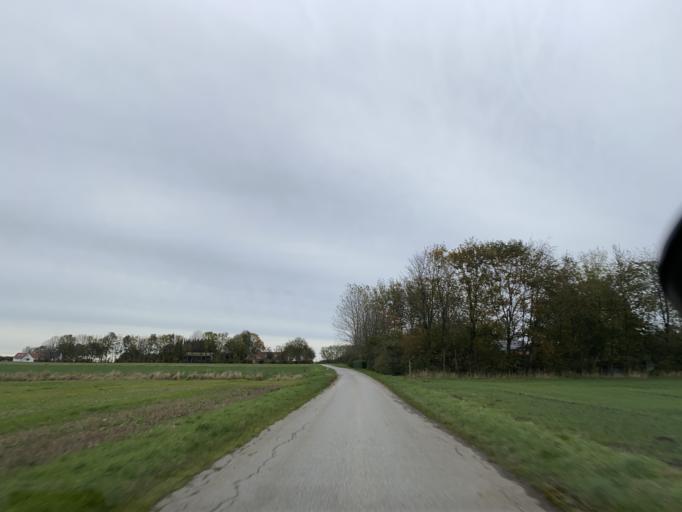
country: DK
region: Central Jutland
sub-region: Skanderborg Kommune
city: Ry
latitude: 56.1865
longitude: 9.7765
